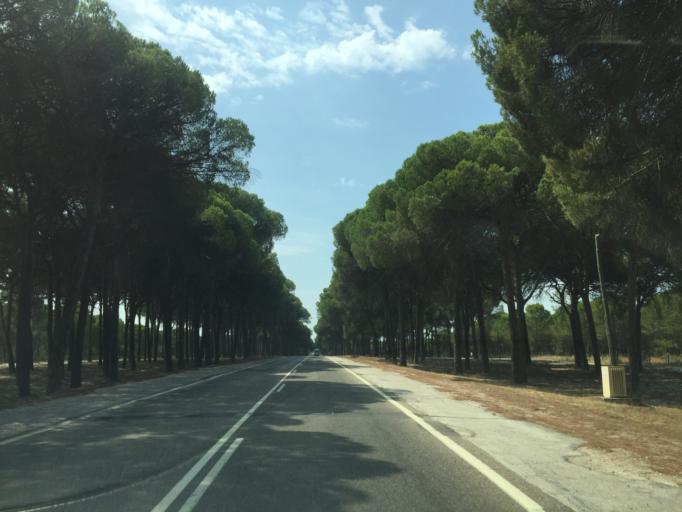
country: PT
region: Setubal
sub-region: Alcacer do Sal
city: Alcacer do Sal
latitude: 38.3350
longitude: -8.5215
